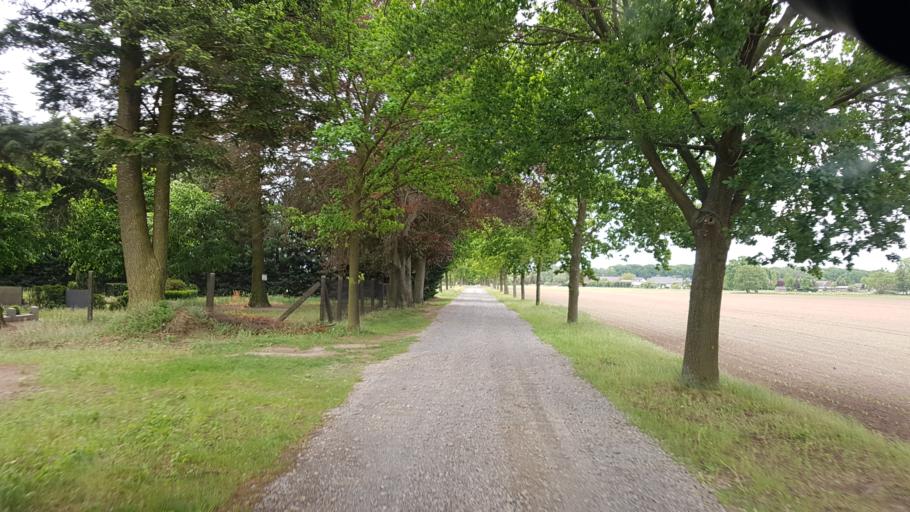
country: DE
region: Brandenburg
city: Schonewalde
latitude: 51.7077
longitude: 13.6025
